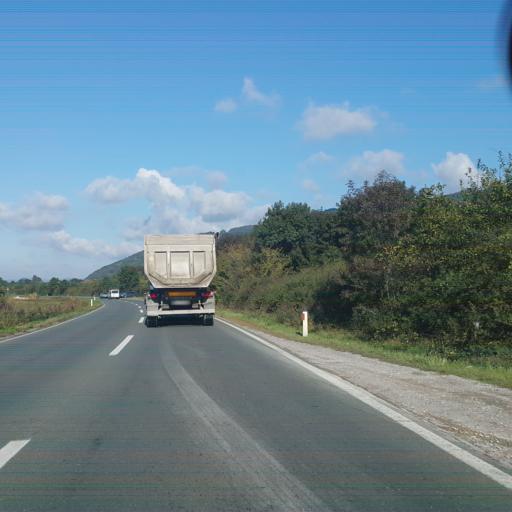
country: RS
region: Central Serbia
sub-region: Rasinski Okrug
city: Trstenik
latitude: 43.6284
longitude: 20.9718
